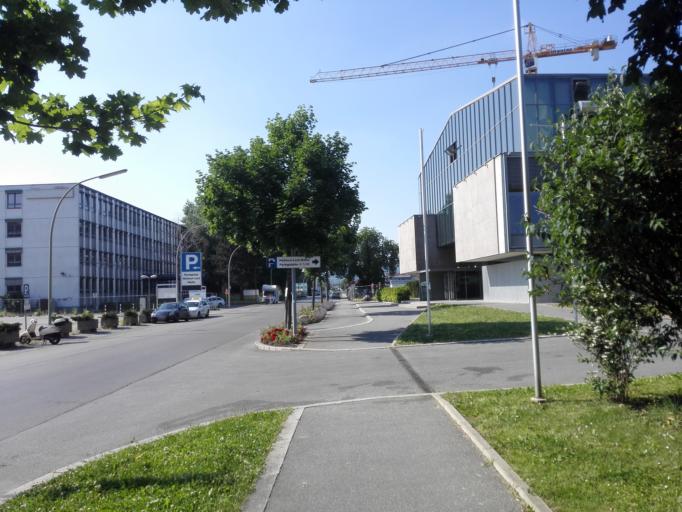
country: AT
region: Styria
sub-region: Graz Stadt
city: Goesting
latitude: 47.0790
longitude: 15.4113
